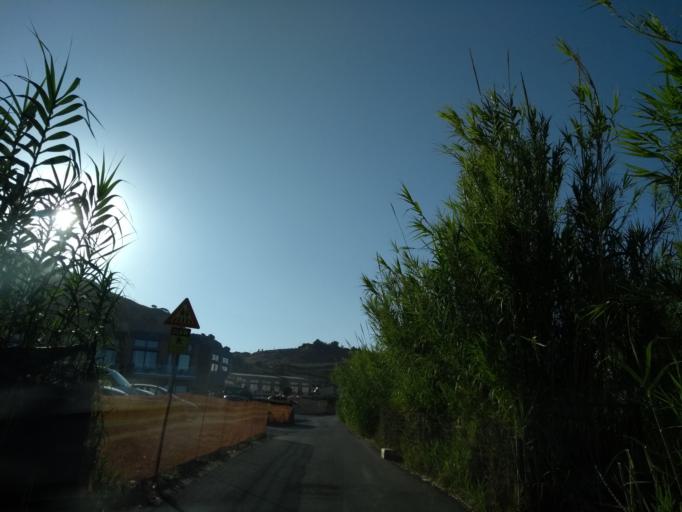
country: GR
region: Crete
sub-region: Nomos Chanias
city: Kalivai
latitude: 35.4650
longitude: 24.1562
